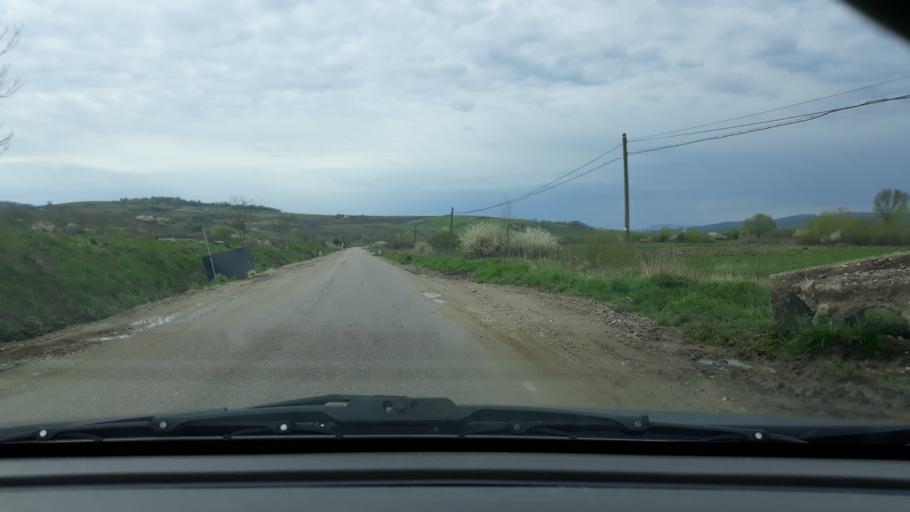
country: RO
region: Salaj
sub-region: Comuna Cehu Silvaniei
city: Cehu Silvaniei
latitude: 47.3972
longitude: 23.1531
